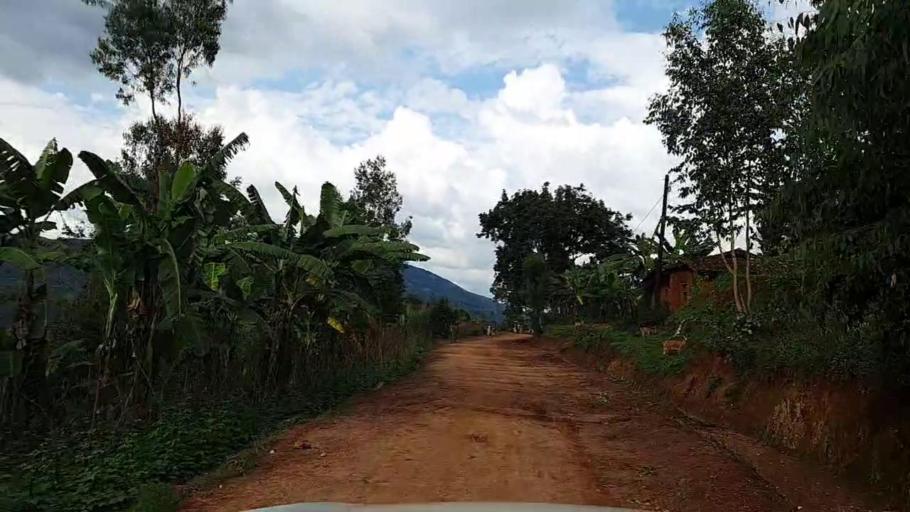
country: RW
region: Southern Province
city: Gikongoro
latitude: -2.4236
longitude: 29.6468
